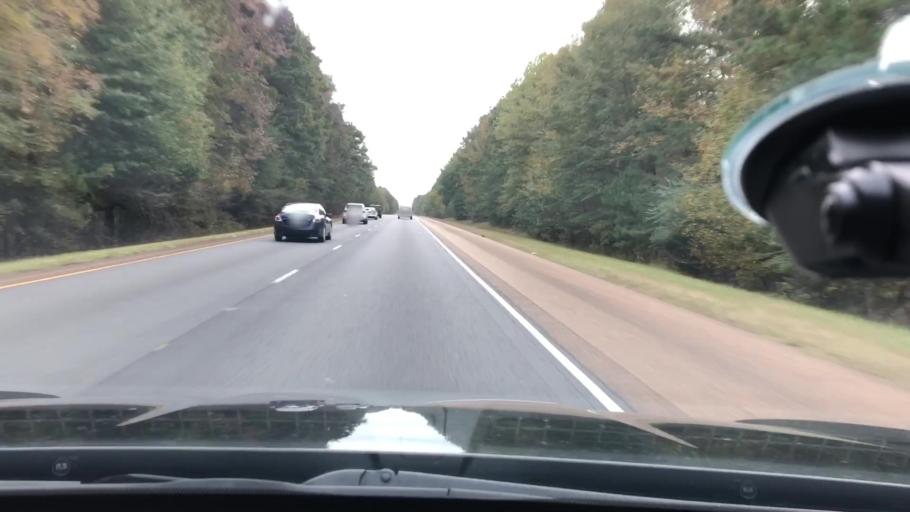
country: US
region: Arkansas
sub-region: Nevada County
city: Prescott
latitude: 33.8578
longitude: -93.3584
